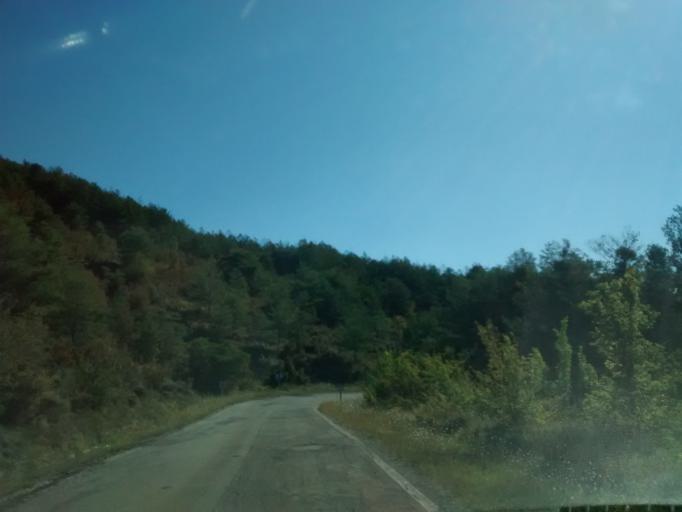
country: ES
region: Aragon
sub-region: Provincia de Huesca
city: Jaca
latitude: 42.5085
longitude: -0.5571
